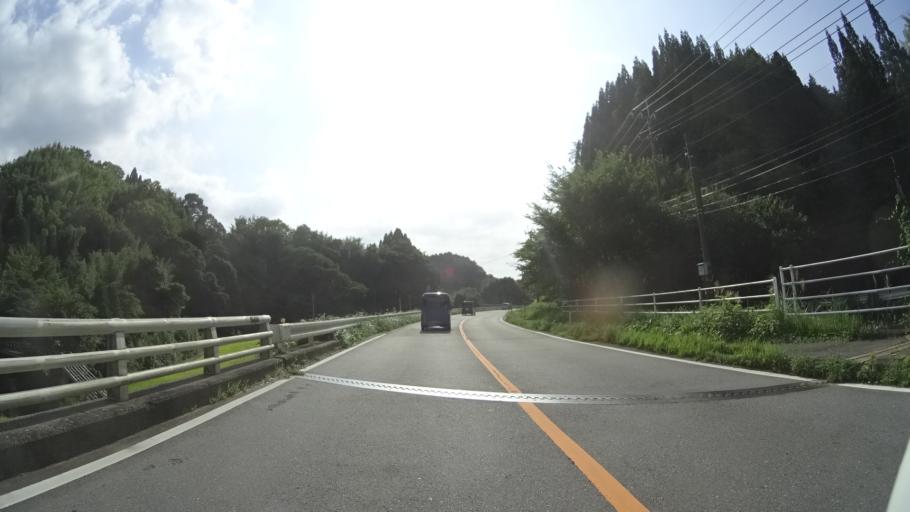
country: JP
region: Kumamoto
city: Aso
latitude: 32.6875
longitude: 131.0685
